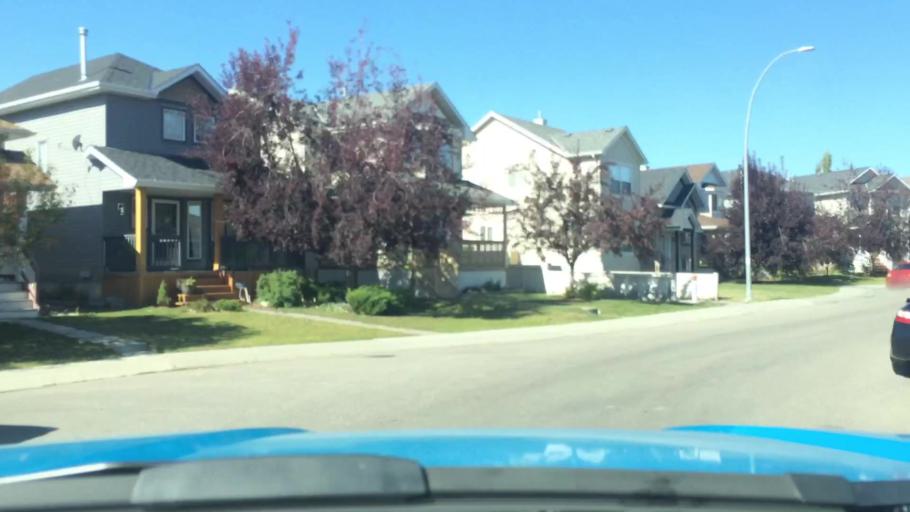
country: CA
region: Alberta
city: Calgary
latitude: 50.9030
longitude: -114.1085
